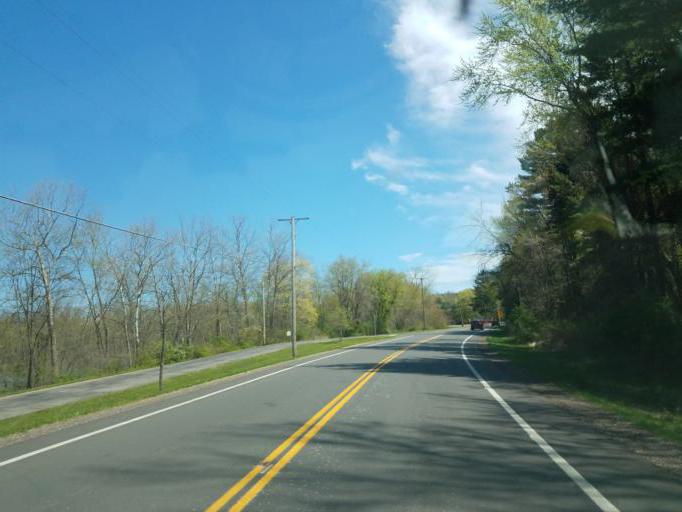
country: US
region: Ohio
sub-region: Richland County
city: Lincoln Heights
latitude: 40.7708
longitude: -82.3750
